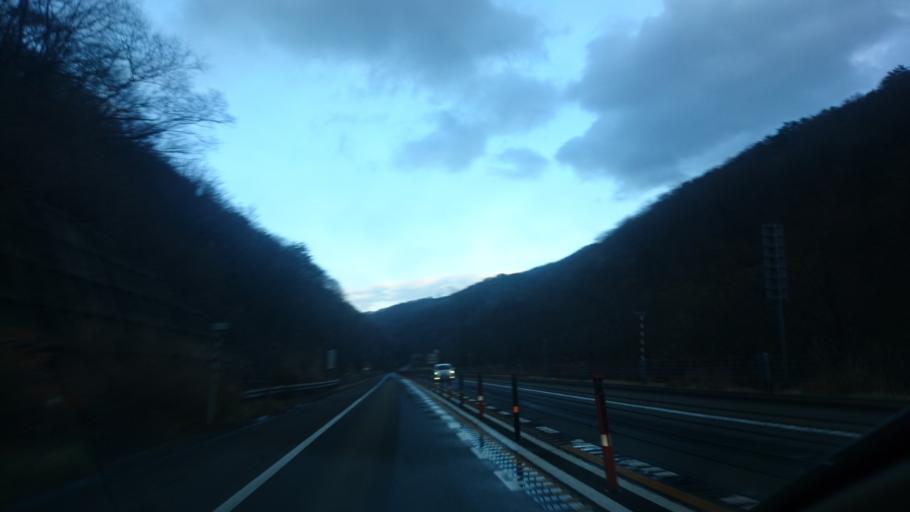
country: JP
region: Iwate
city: Kitakami
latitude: 39.2912
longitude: 140.8647
